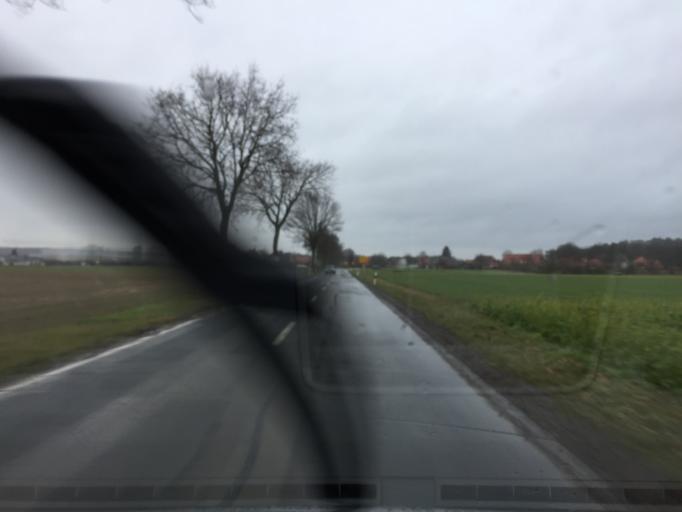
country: DE
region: Lower Saxony
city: Steyerberg
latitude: 52.5582
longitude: 9.0284
